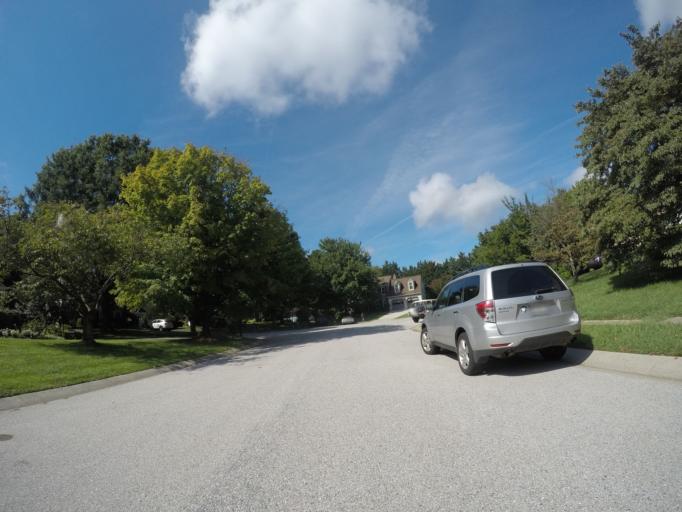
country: US
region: Maryland
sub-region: Howard County
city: Columbia
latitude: 39.2660
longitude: -76.8638
